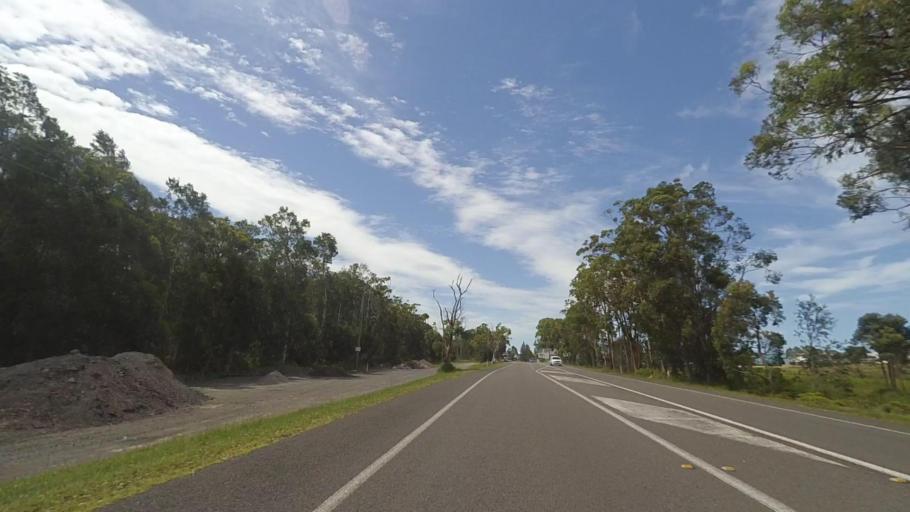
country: AU
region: New South Wales
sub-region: Port Stephens Shire
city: Anna Bay
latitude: -32.7550
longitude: 152.0683
